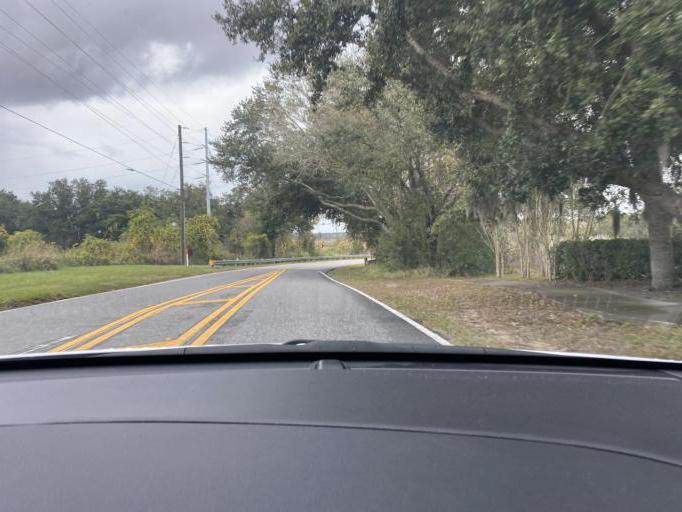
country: US
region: Florida
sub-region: Lake County
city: Minneola
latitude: 28.5947
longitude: -81.7860
